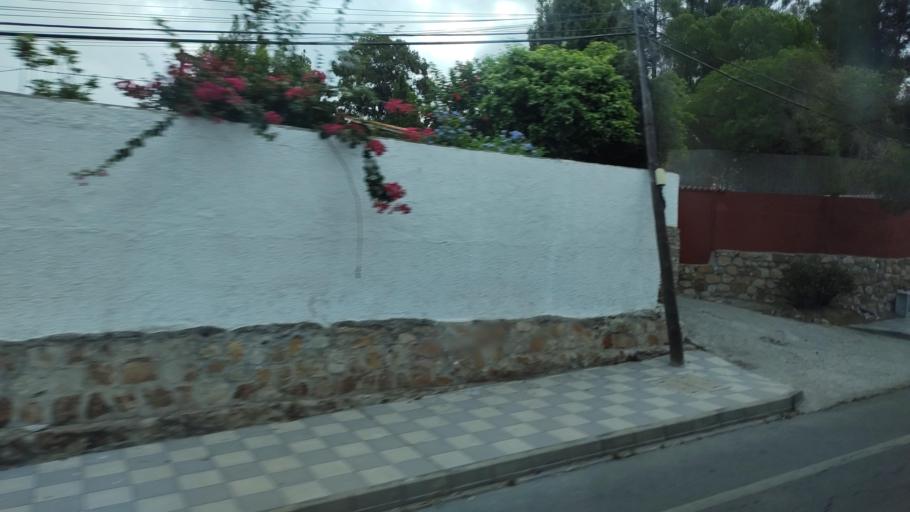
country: ES
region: Andalusia
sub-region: Provincia de Cadiz
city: San Roque
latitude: 36.1794
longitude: -5.3791
